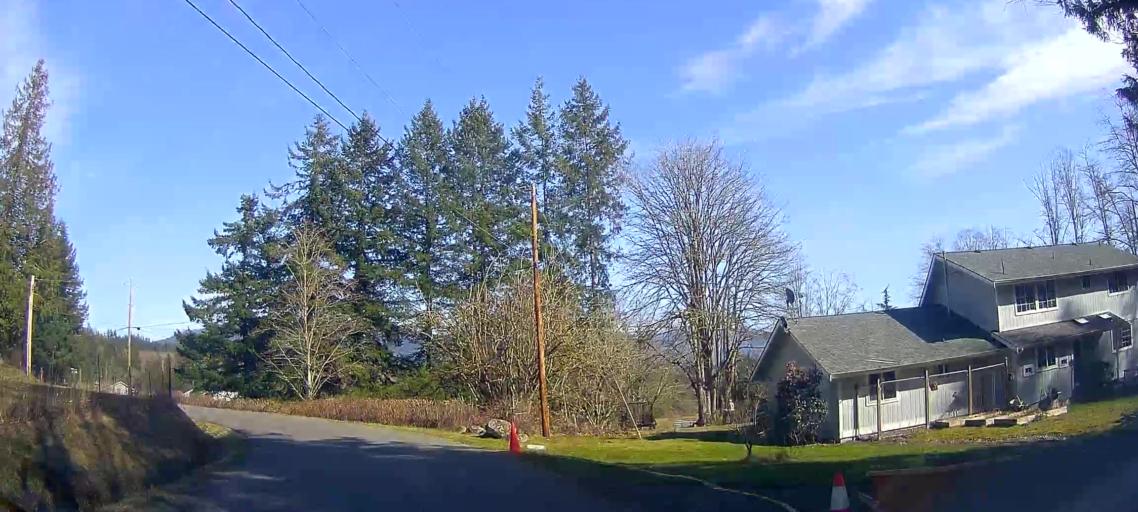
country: US
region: Washington
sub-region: Skagit County
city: Burlington
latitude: 48.5892
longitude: -122.3709
